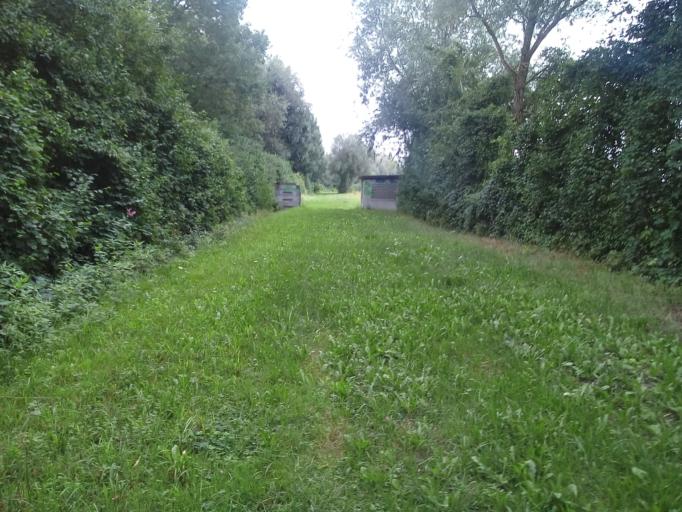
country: DE
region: Bavaria
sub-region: Upper Bavaria
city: Ismaning
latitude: 48.2071
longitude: 11.6954
